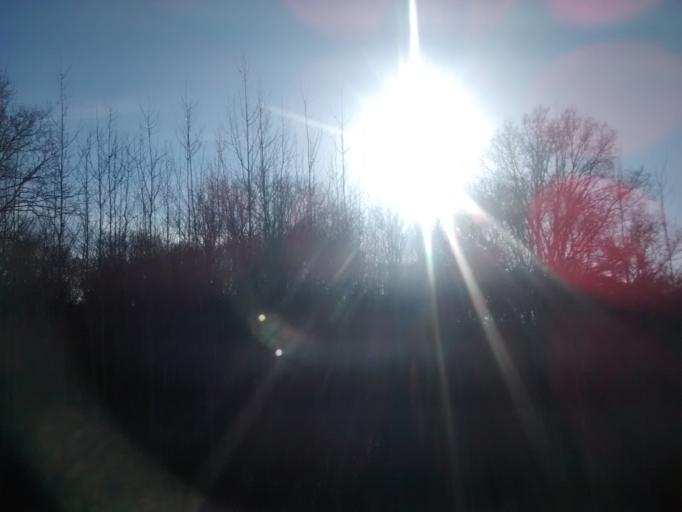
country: NL
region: North Brabant
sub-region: Gemeente Best
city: Best
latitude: 51.5403
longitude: 5.3611
